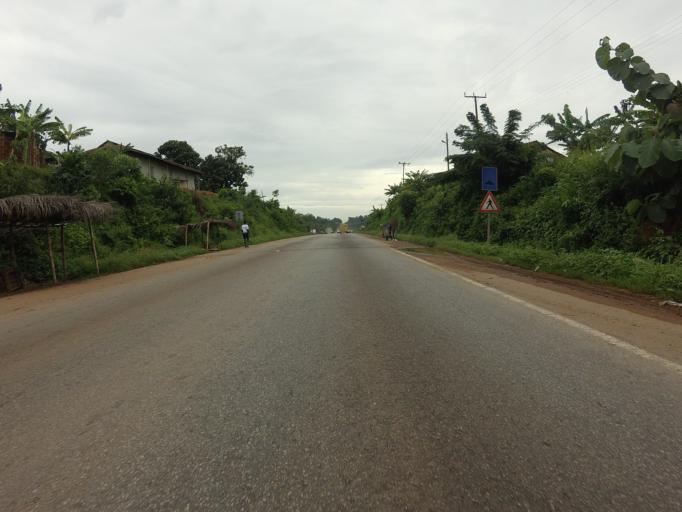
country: GH
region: Eastern
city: Nkawkaw
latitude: 6.4793
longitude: -0.6603
